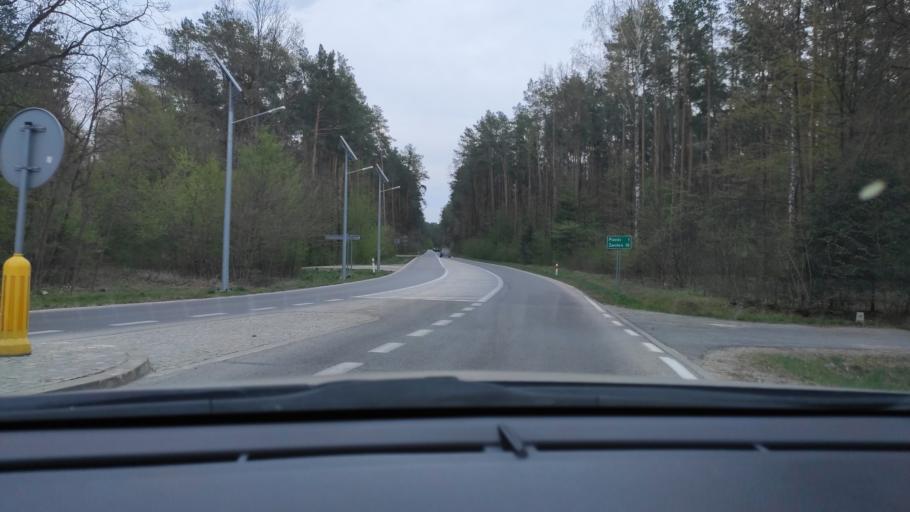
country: PL
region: Masovian Voivodeship
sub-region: Powiat radomski
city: Pionki
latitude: 51.4920
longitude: 21.4221
